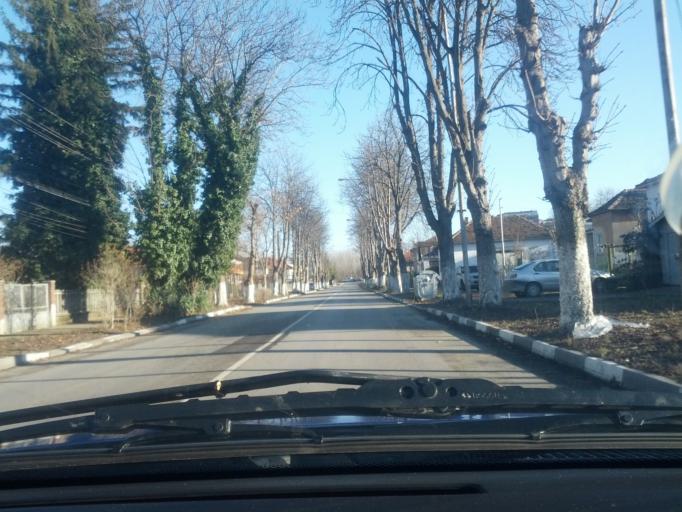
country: BG
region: Vratsa
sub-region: Obshtina Kozloduy
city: Kozloduy
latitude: 43.7858
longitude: 23.7178
